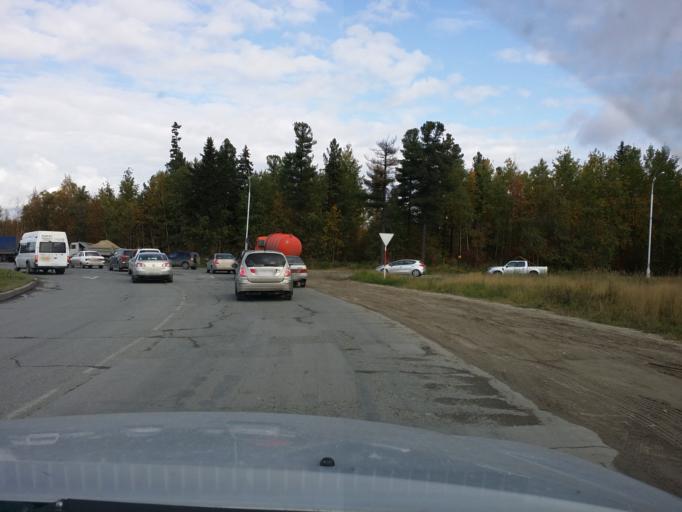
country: RU
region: Khanty-Mansiyskiy Avtonomnyy Okrug
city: Nizhnevartovsk
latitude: 60.9693
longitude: 76.5328
